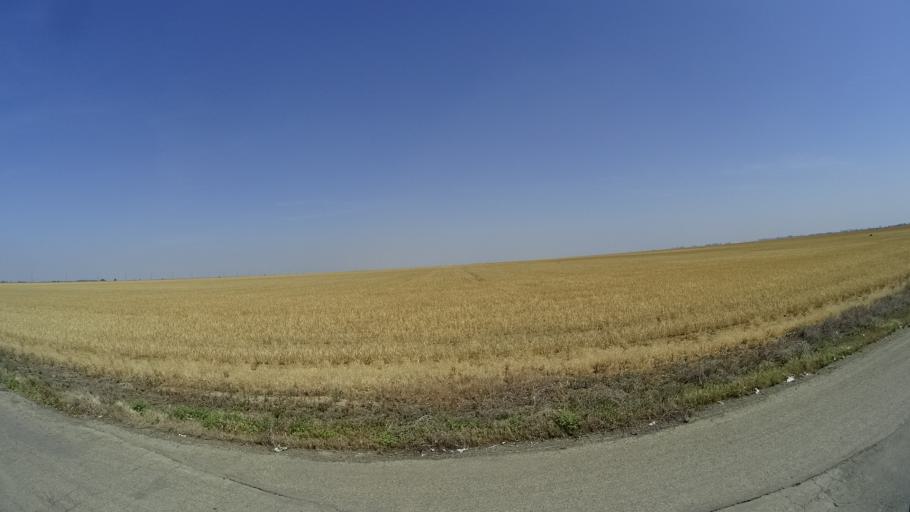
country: US
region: California
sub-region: Kings County
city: Stratford
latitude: 36.1378
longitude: -119.8974
